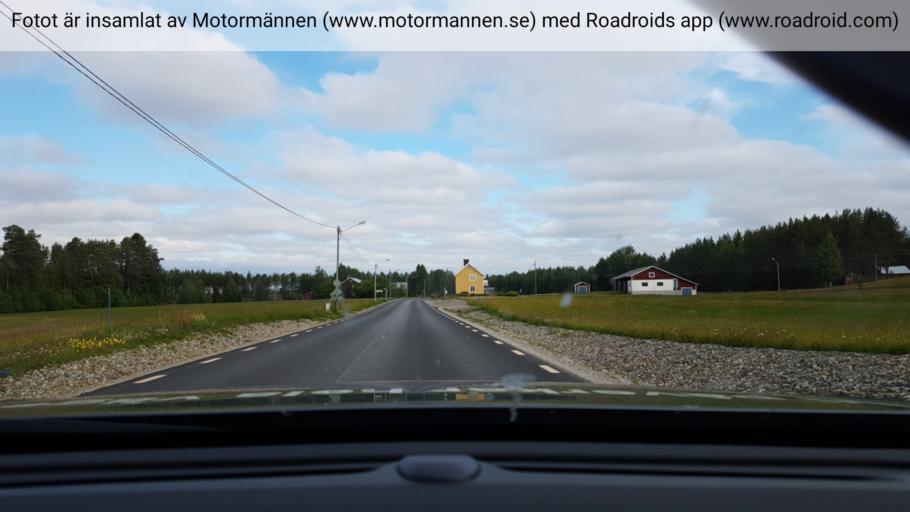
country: SE
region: Vaesterbotten
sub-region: Norsjo Kommun
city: Norsjoe
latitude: 64.5396
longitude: 19.3377
